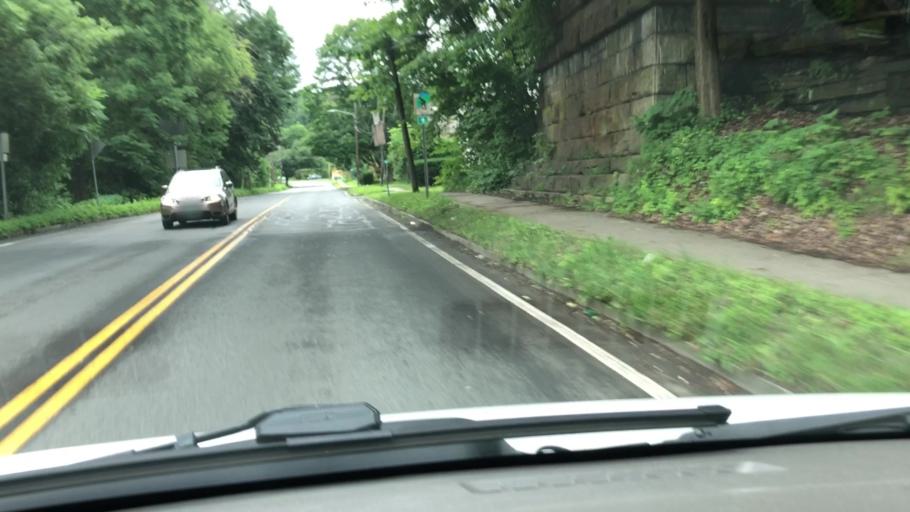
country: US
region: Massachusetts
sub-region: Franklin County
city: Greenfield
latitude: 42.5851
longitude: -72.6124
